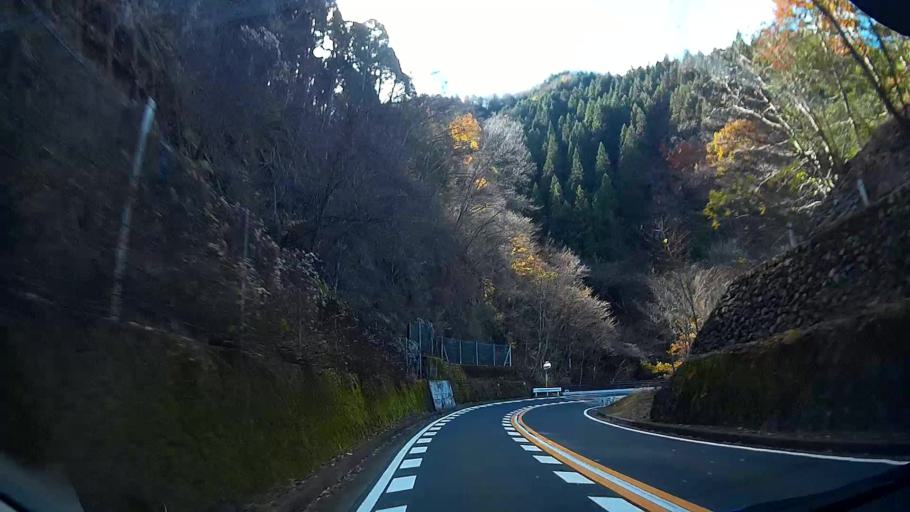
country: JP
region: Yamanashi
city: Uenohara
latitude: 35.7546
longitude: 139.0367
